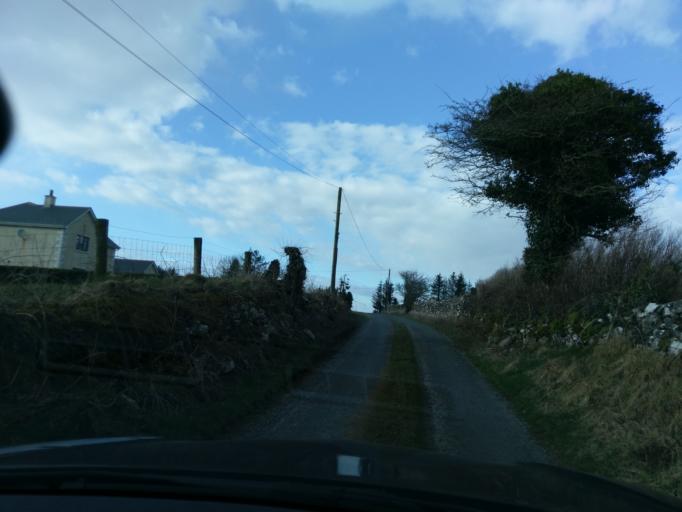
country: IE
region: Connaught
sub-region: County Galway
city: Athenry
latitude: 53.4519
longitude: -8.6420
